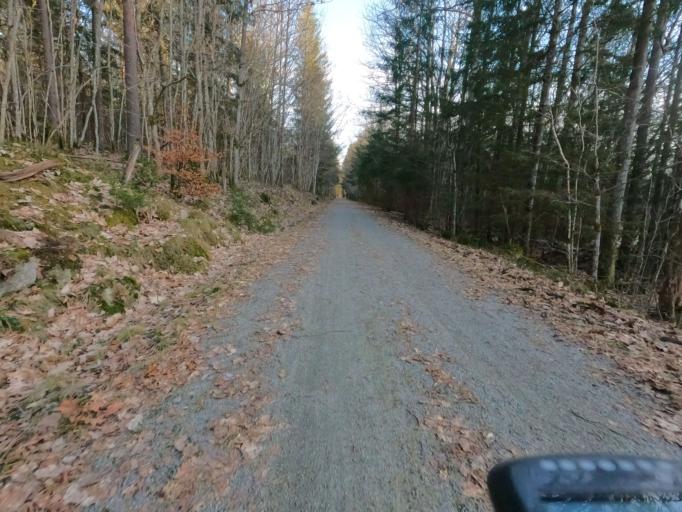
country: SE
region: Blekinge
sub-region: Karlshamns Kommun
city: Svangsta
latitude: 56.3783
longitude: 14.6794
